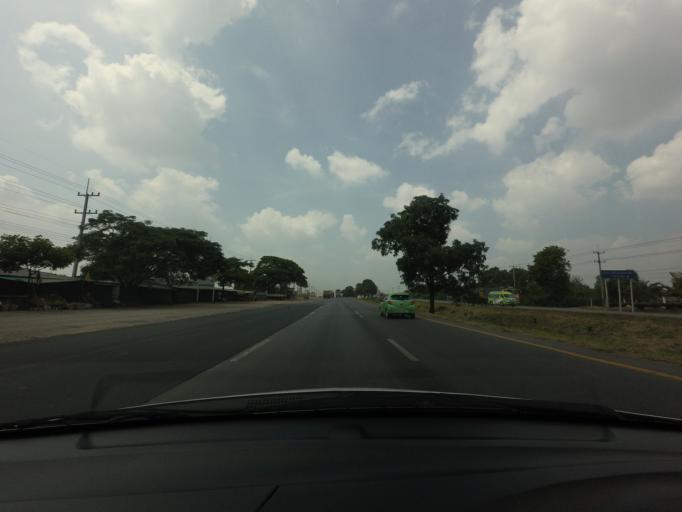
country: TH
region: Nakhon Ratchasima
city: Pak Chong
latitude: 14.6679
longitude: 101.4404
